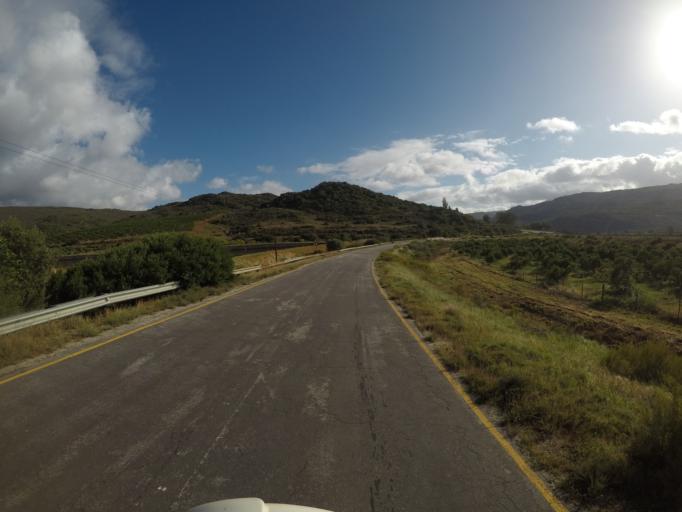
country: ZA
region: Western Cape
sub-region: West Coast District Municipality
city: Clanwilliam
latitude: -32.4320
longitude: 18.9538
